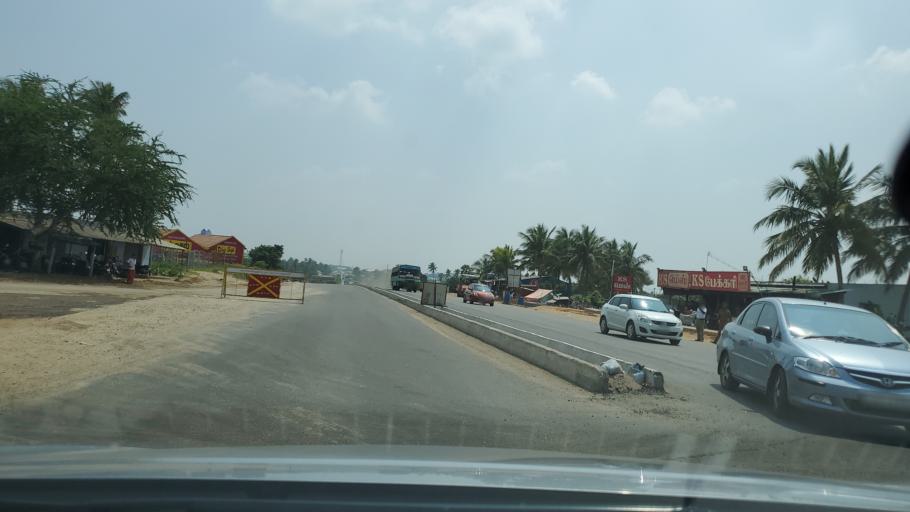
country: IN
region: Tamil Nadu
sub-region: Tiruppur
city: Dharapuram
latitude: 10.7762
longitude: 77.5069
